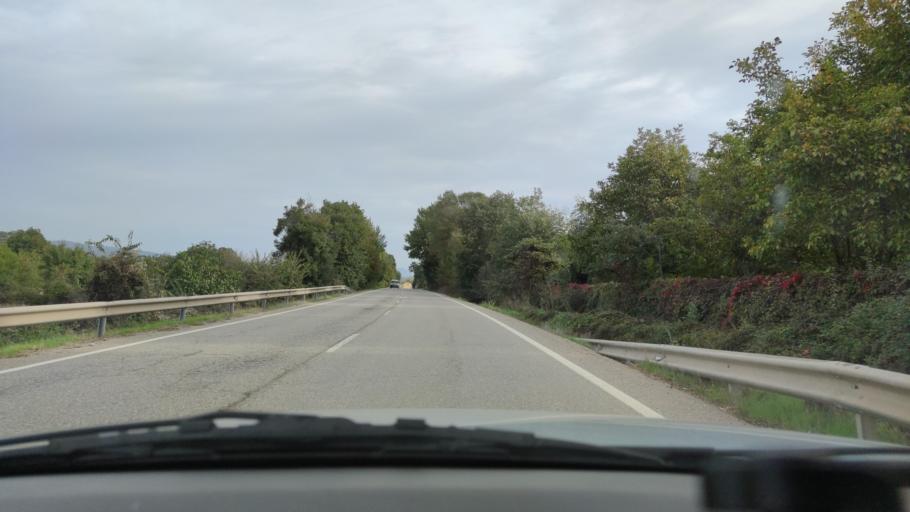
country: ES
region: Catalonia
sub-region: Provincia de Lleida
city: Artesa de Segre
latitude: 41.9026
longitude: 1.0652
